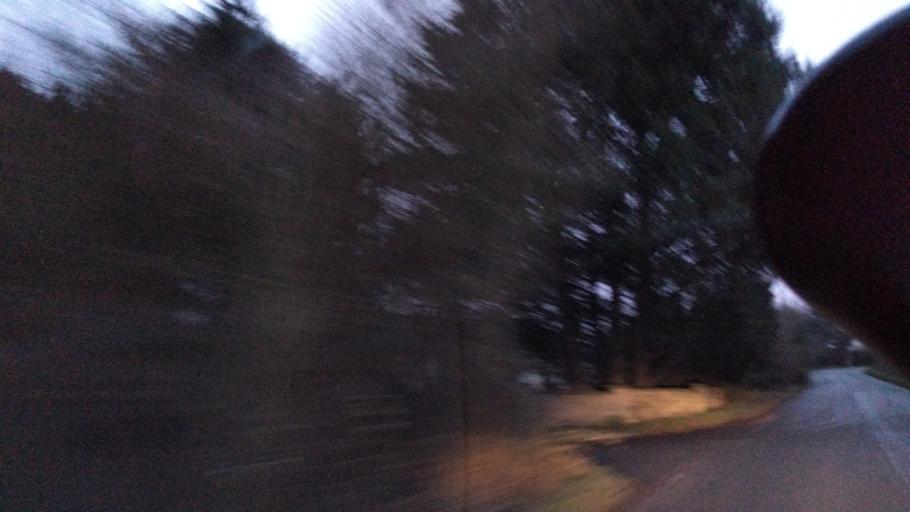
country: GB
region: England
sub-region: Borough of Swindon
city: Wanborough
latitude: 51.5820
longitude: -1.7272
